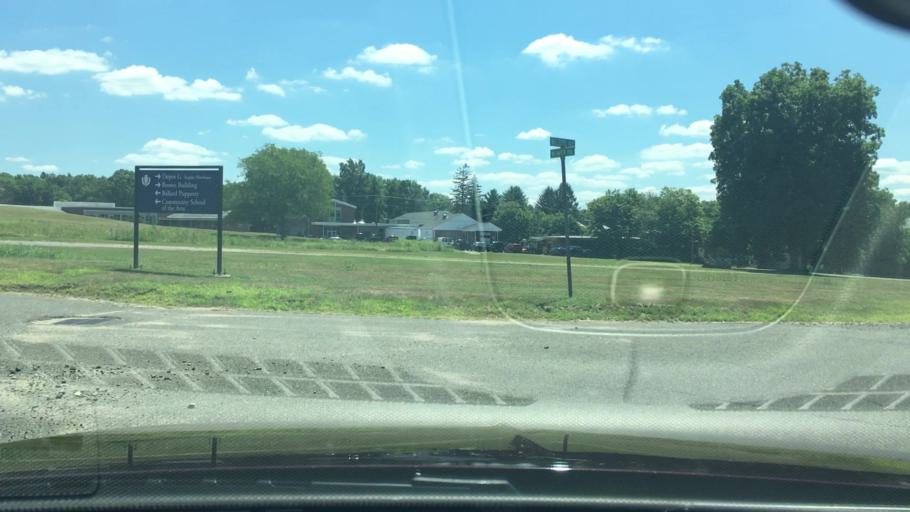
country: US
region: Connecticut
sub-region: Tolland County
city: South Coventry
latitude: 41.8093
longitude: -72.2960
